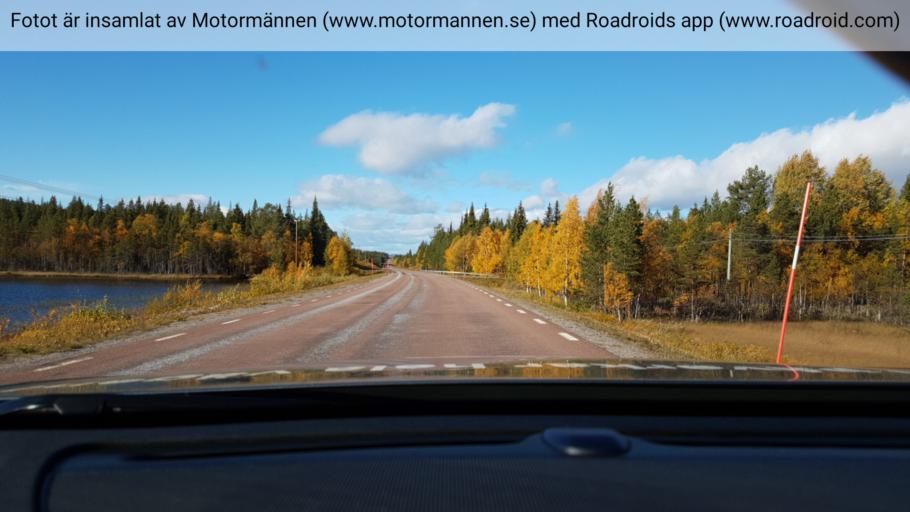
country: SE
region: Norrbotten
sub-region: Arjeplogs Kommun
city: Arjeplog
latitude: 66.0514
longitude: 18.0178
